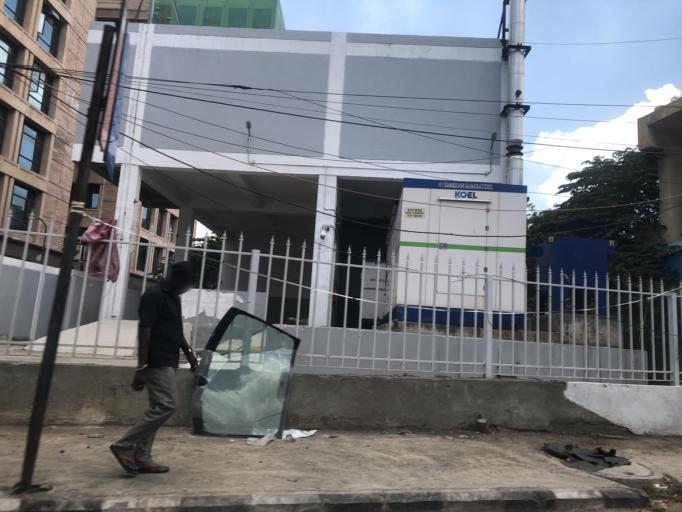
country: IN
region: Tamil Nadu
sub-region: Chennai
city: Chennai
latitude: 13.0643
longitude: 80.2674
